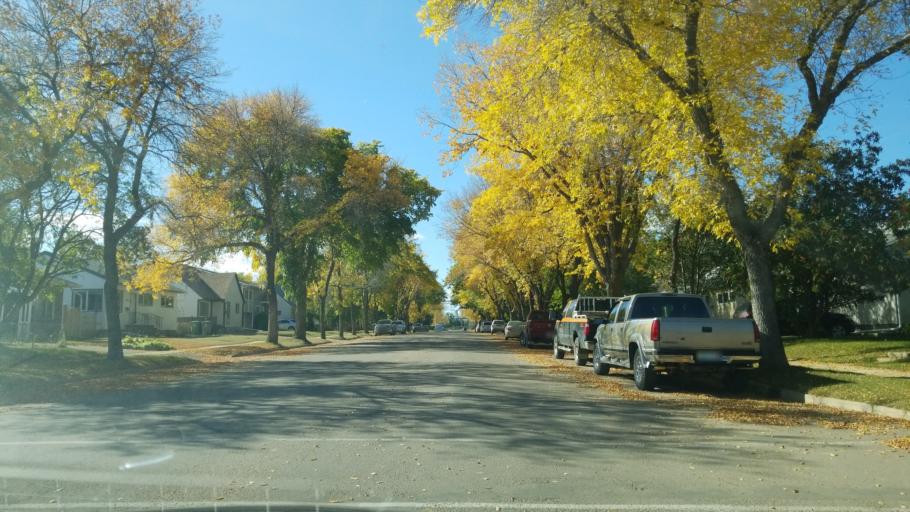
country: CA
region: Saskatchewan
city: Lloydminster
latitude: 53.2835
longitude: -110.0204
